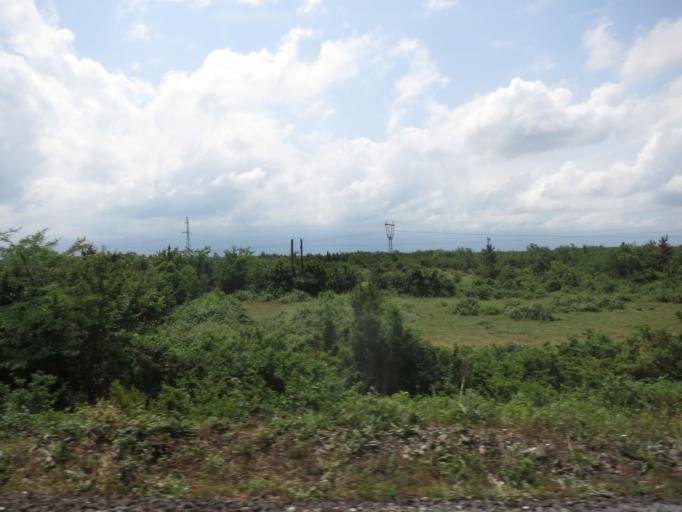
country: GE
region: Imereti
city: Kutaisi
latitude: 42.1995
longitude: 42.6464
